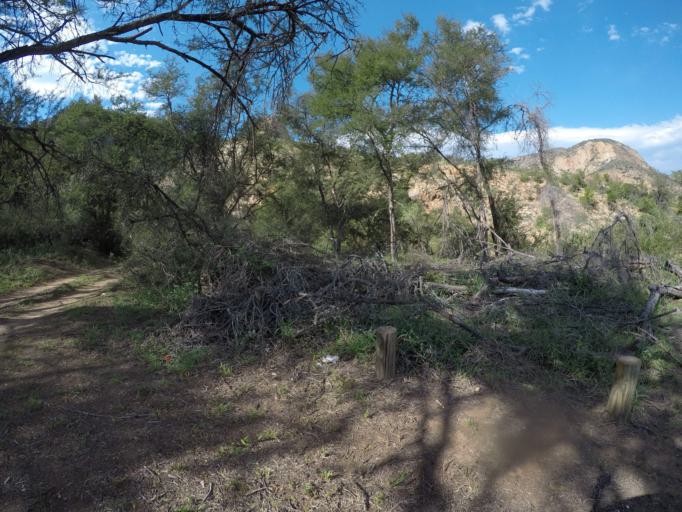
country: ZA
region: Eastern Cape
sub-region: Cacadu District Municipality
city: Kareedouw
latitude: -33.6586
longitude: 24.4322
